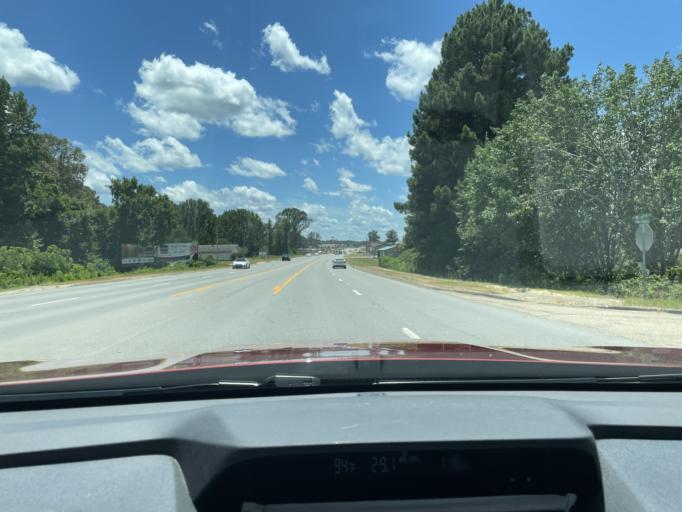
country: US
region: Arkansas
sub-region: Drew County
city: Monticello
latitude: 33.6447
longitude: -91.8010
